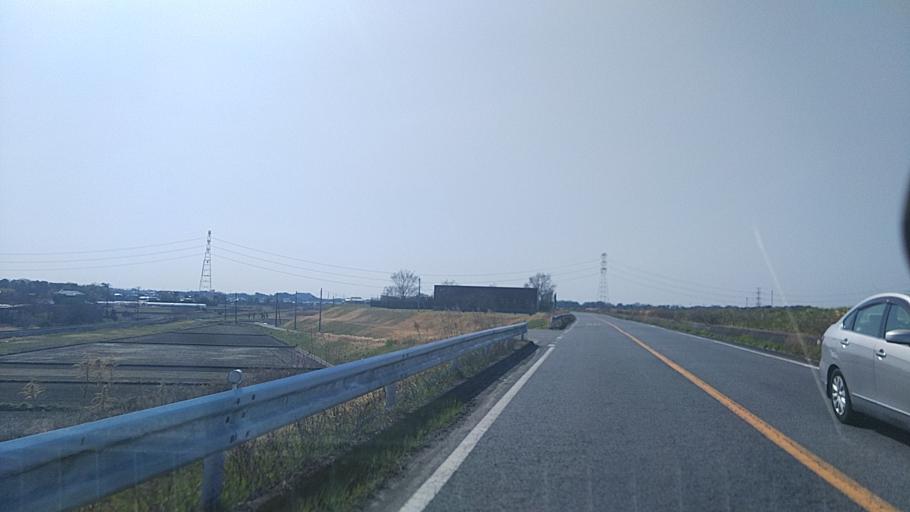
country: JP
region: Ibaraki
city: Fujishiro
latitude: 35.8773
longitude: 140.1277
